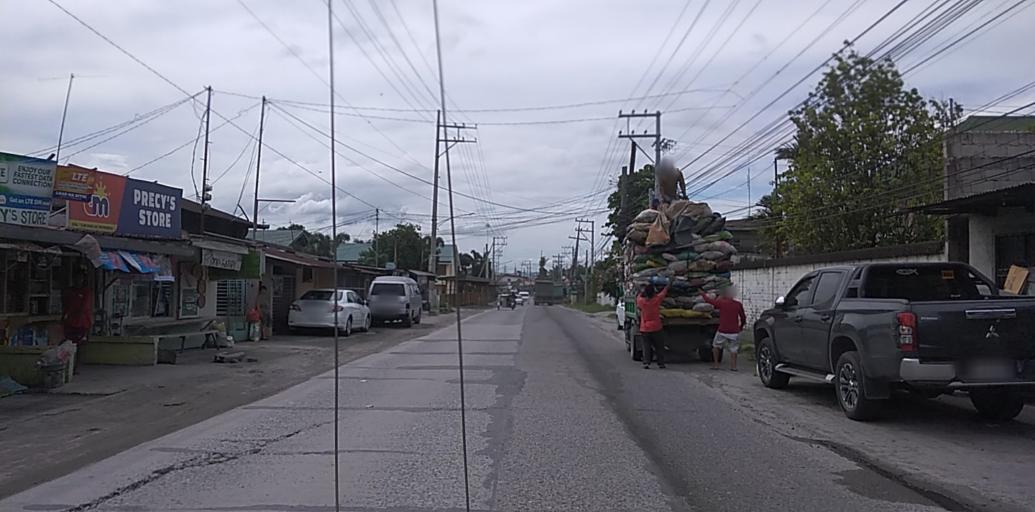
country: PH
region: Central Luzon
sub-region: Province of Pampanga
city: Manibaug Pasig
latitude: 15.1084
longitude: 120.5628
